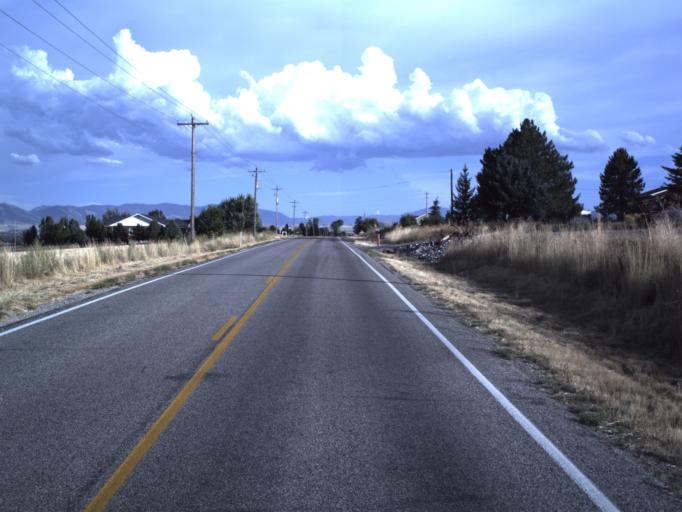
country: US
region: Utah
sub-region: Cache County
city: Wellsville
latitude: 41.6725
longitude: -111.9552
